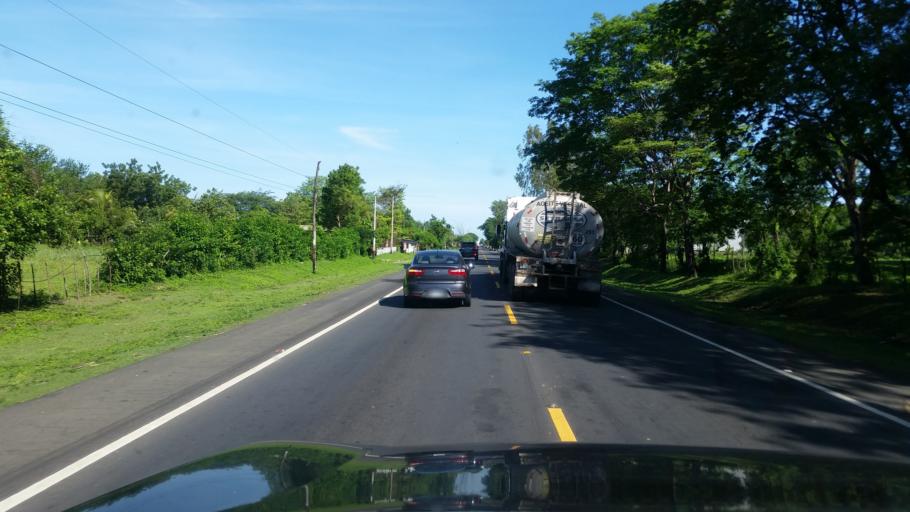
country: NI
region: Chinandega
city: Posoltega
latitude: 12.5715
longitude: -86.9801
